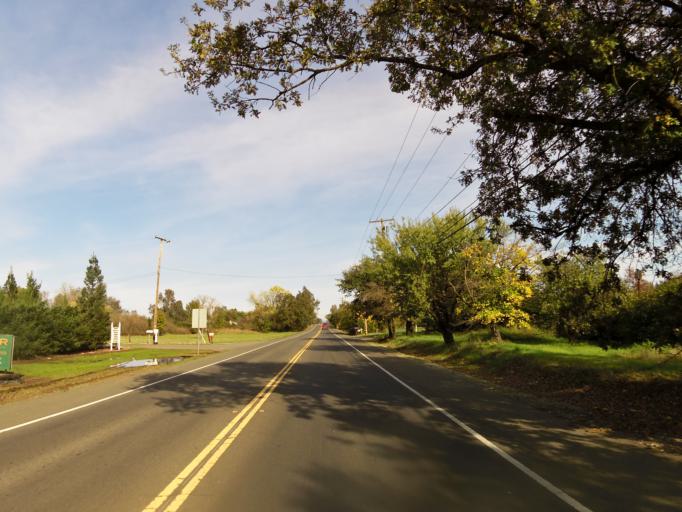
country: US
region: California
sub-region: Sacramento County
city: Wilton
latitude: 38.4389
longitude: -121.2918
